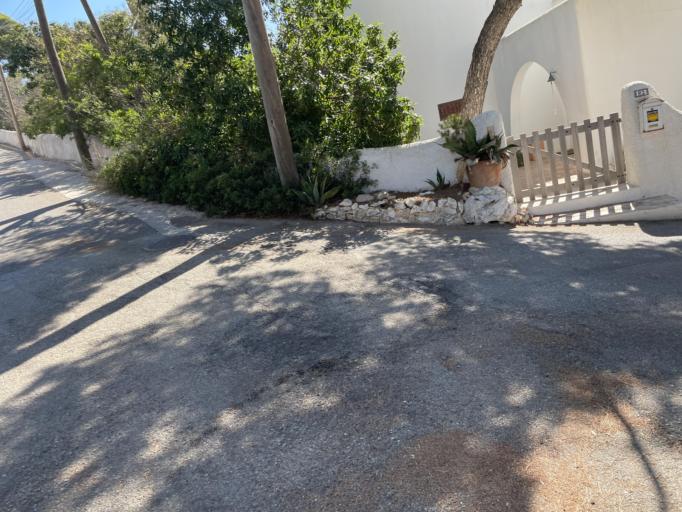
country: ES
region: Balearic Islands
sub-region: Illes Balears
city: Capdepera
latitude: 39.7189
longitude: 3.4688
